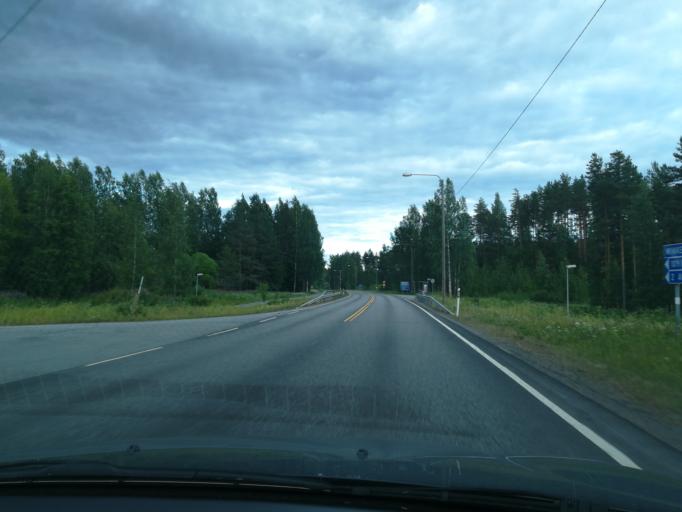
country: FI
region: Southern Savonia
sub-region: Mikkeli
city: Mikkeli
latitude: 61.5891
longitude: 27.6180
